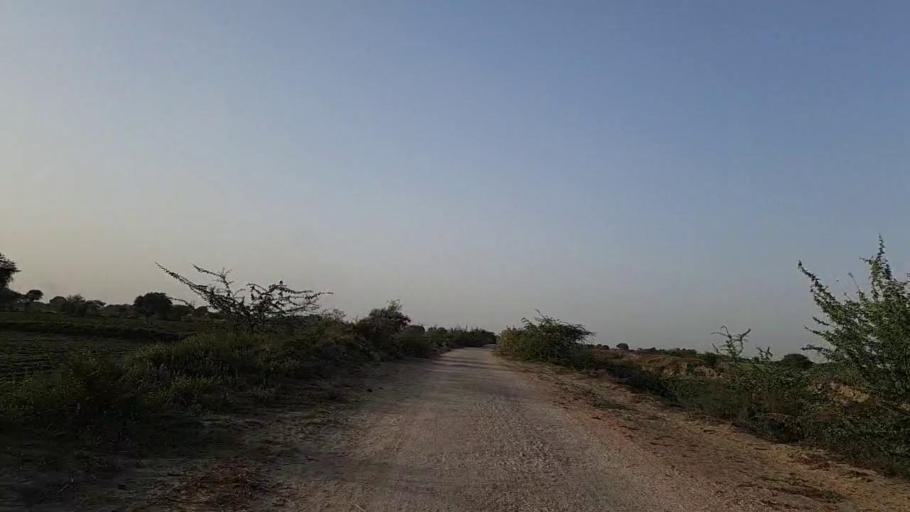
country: PK
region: Sindh
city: Jati
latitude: 24.4028
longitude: 68.1872
